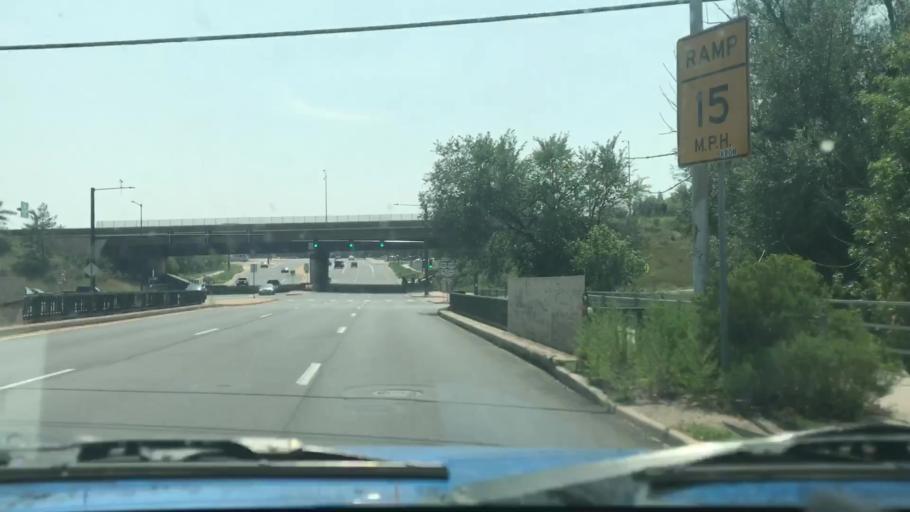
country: US
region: Colorado
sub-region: Arapahoe County
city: Sheridan
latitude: 39.6546
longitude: -105.0534
